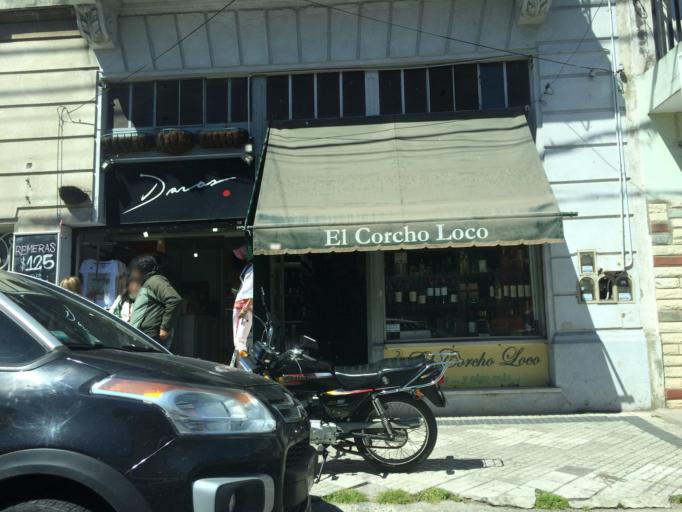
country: AR
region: Buenos Aires
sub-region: Partido de Lanus
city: Lanus
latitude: -34.7256
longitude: -58.3985
